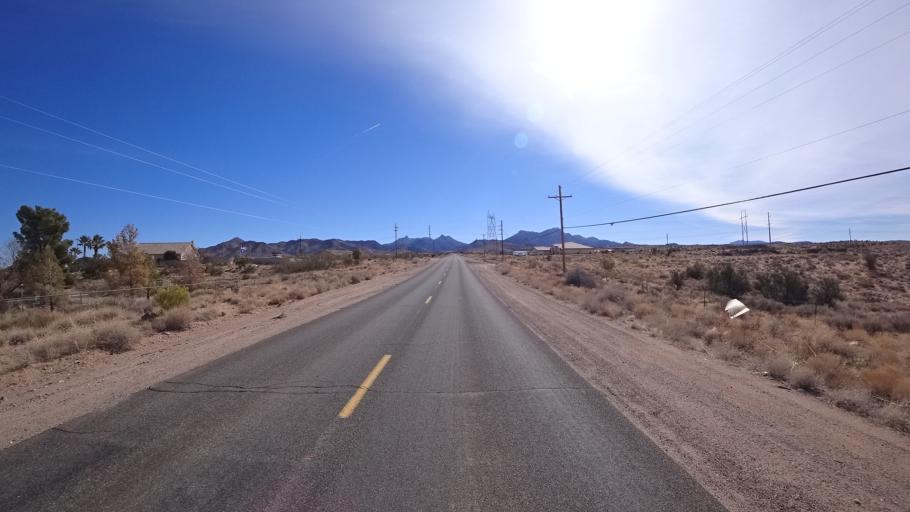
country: US
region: Arizona
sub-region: Mohave County
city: Kingman
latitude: 35.1765
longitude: -113.9893
